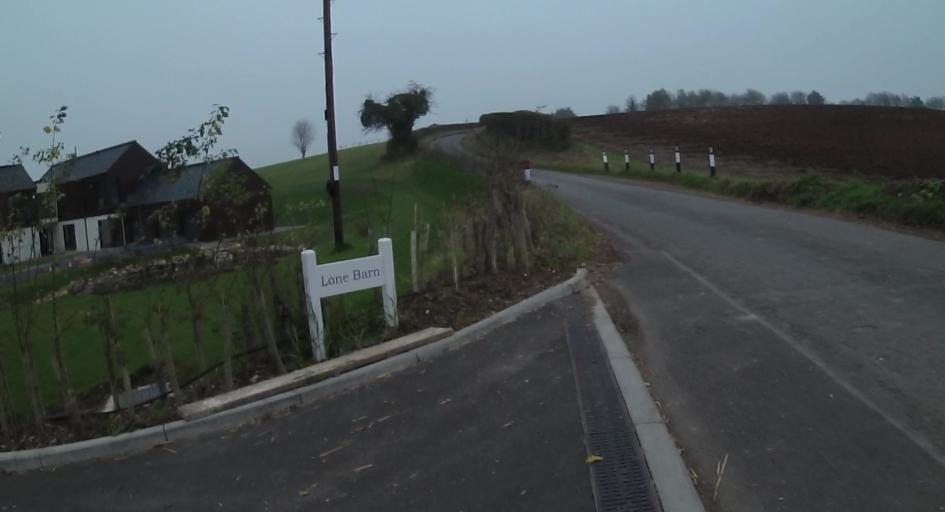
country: GB
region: England
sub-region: Hampshire
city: Kings Worthy
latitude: 51.0806
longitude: -1.2827
